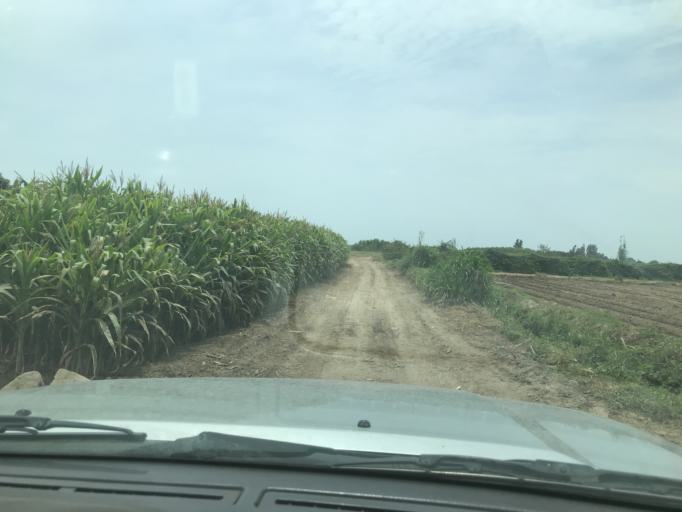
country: PE
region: La Libertad
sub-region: Viru
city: Viru
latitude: -8.4209
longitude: -78.7917
